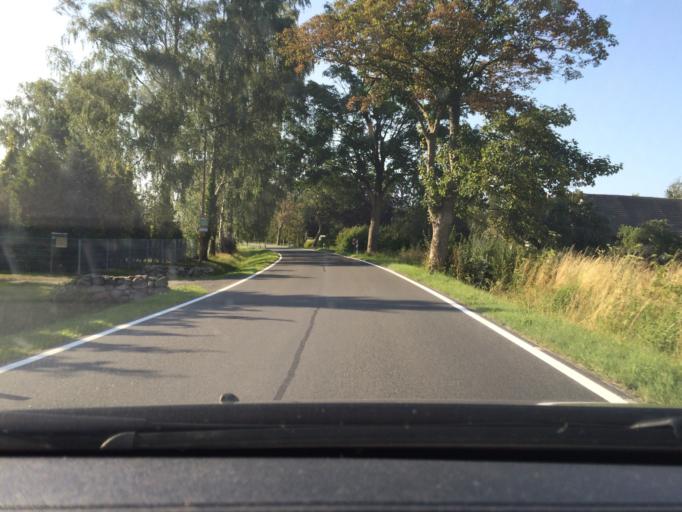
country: DE
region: Mecklenburg-Vorpommern
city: Niepars
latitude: 54.3337
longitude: 12.9327
